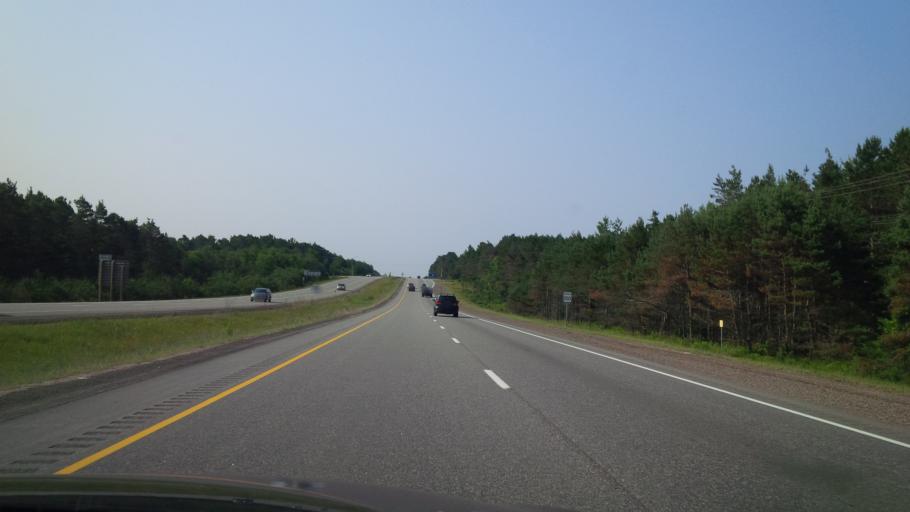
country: CA
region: Ontario
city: Bracebridge
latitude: 45.0768
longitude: -79.2969
